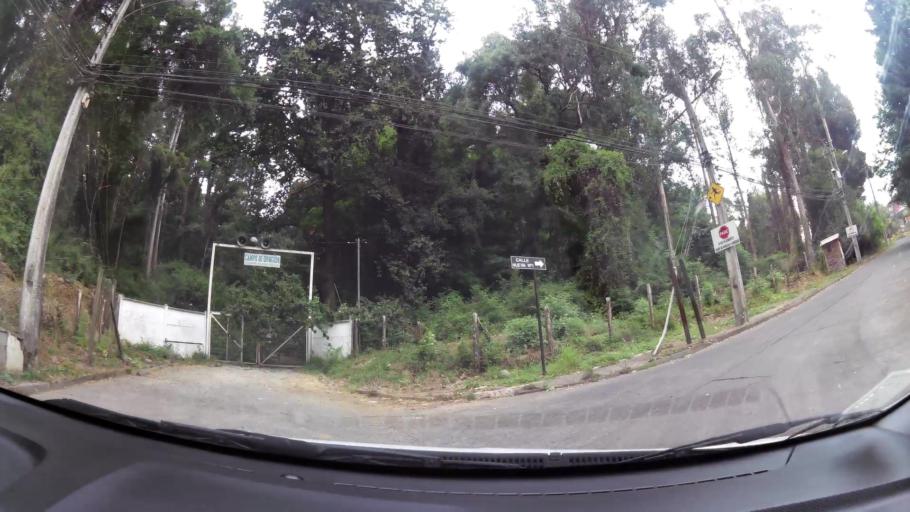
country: CL
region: Biobio
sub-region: Provincia de Concepcion
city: Concepcion
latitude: -36.8238
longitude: -73.0299
